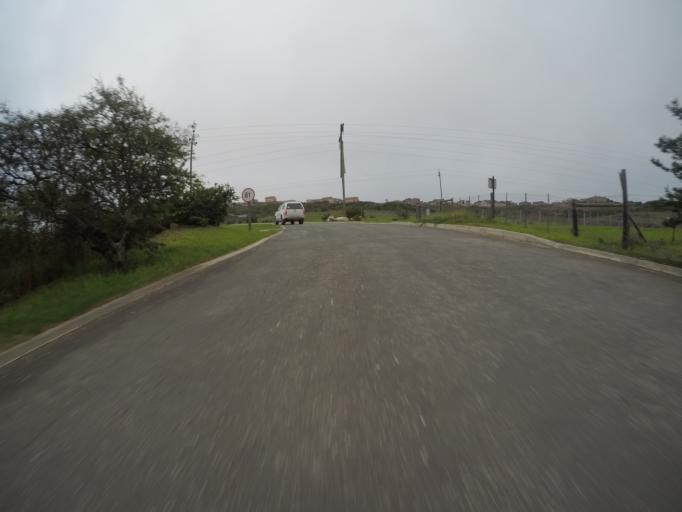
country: ZA
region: Western Cape
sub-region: Eden District Municipality
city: Mossel Bay
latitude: -34.1423
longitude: 22.0893
